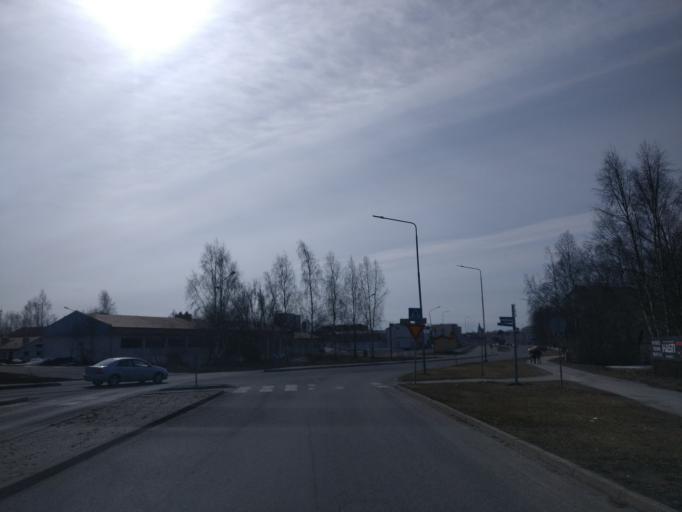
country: FI
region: Lapland
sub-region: Kemi-Tornio
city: Kemi
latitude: 65.7433
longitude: 24.5661
